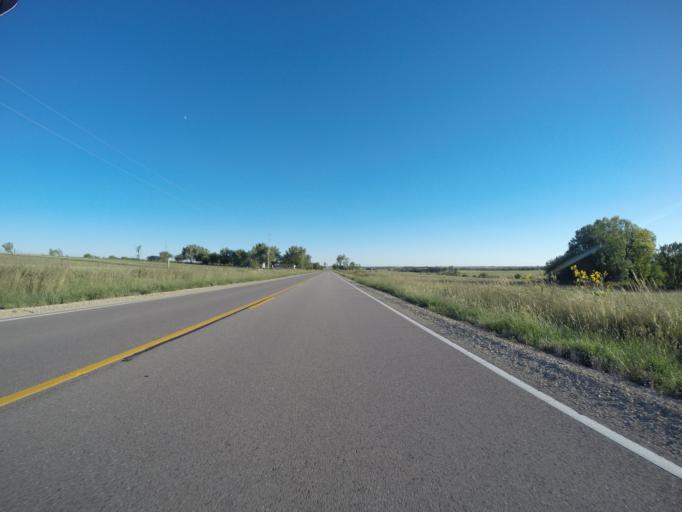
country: US
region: Kansas
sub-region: Riley County
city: Fort Riley North
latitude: 39.2824
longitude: -96.7751
